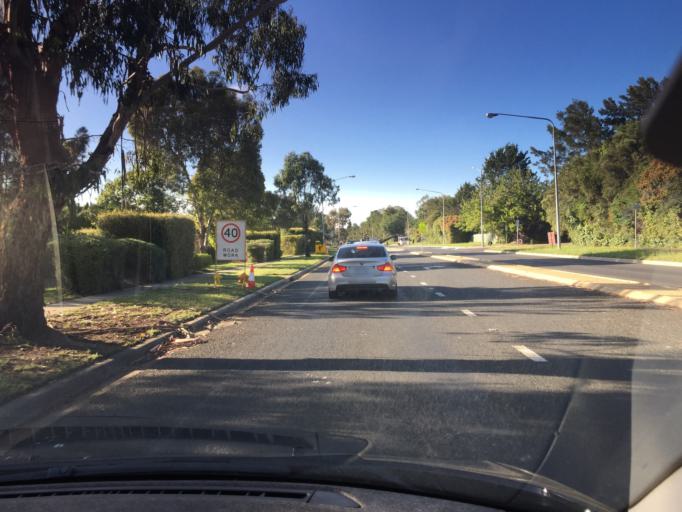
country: AU
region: Australian Capital Territory
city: Kaleen
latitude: -35.2359
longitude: 149.1254
